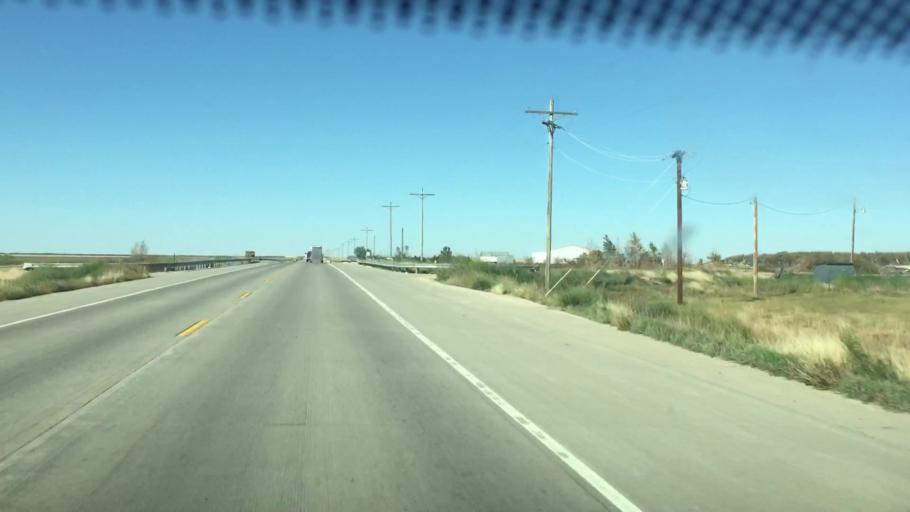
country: US
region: Colorado
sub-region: Prowers County
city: Lamar
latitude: 38.2279
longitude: -102.7240
